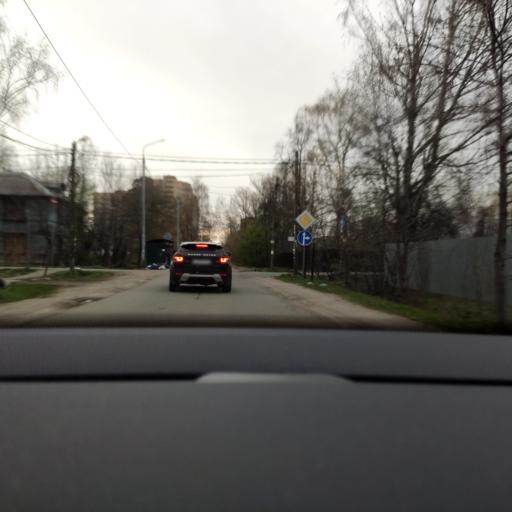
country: RU
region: Moskovskaya
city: Reutov
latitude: 55.7710
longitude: 37.8886
